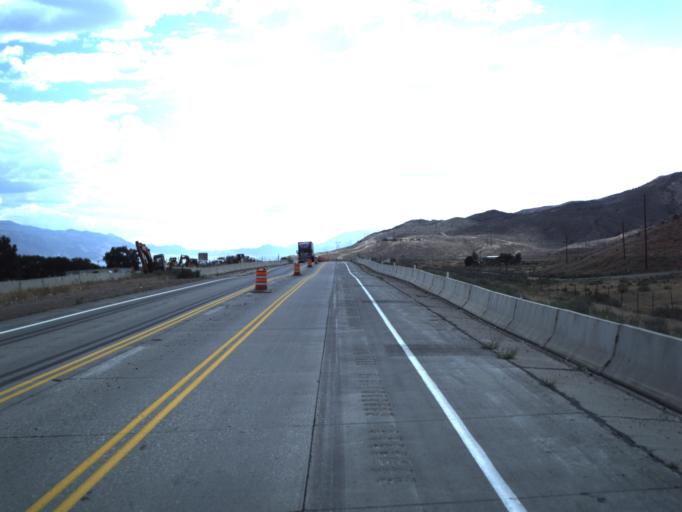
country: US
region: Utah
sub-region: Sevier County
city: Richfield
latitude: 38.7738
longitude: -112.0985
